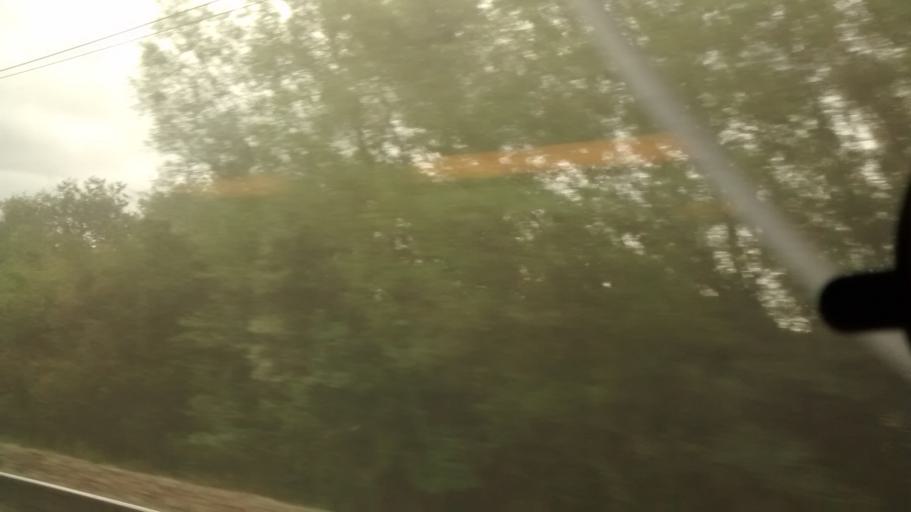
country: FR
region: Ile-de-France
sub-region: Departement de l'Essonne
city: Vaugrigneuse
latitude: 48.6119
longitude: 2.1153
